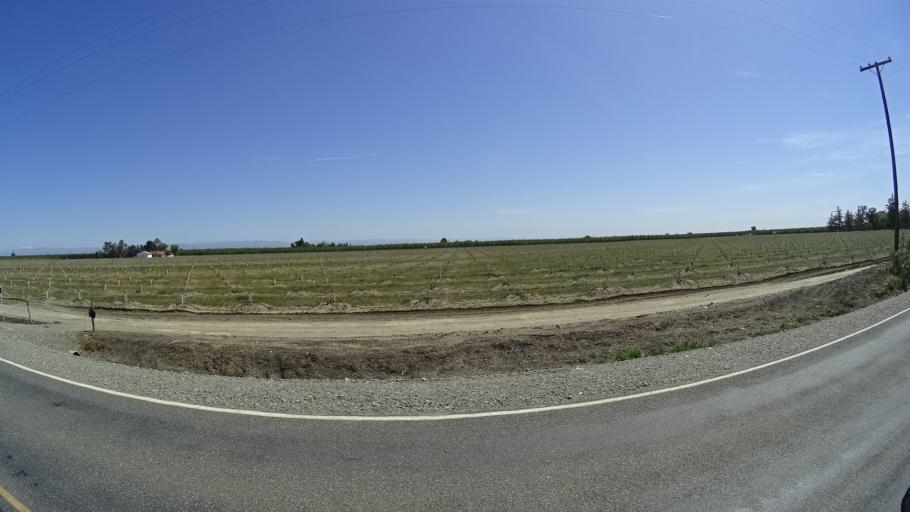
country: US
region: California
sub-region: Glenn County
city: Orland
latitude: 39.7071
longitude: -122.1415
